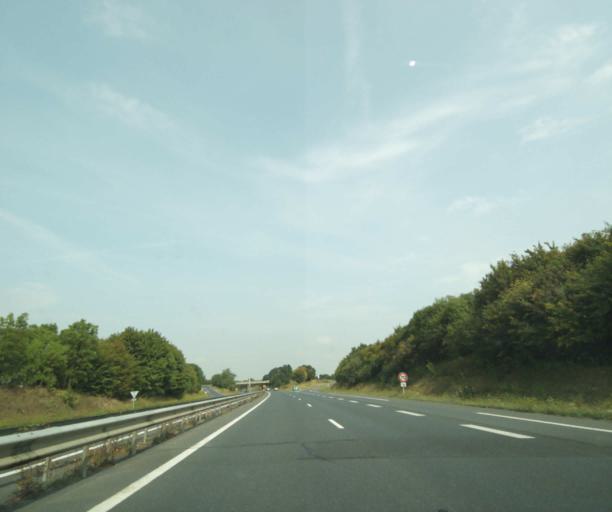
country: FR
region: Lower Normandy
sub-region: Departement du Calvados
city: Potigny
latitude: 49.0130
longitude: -0.2618
